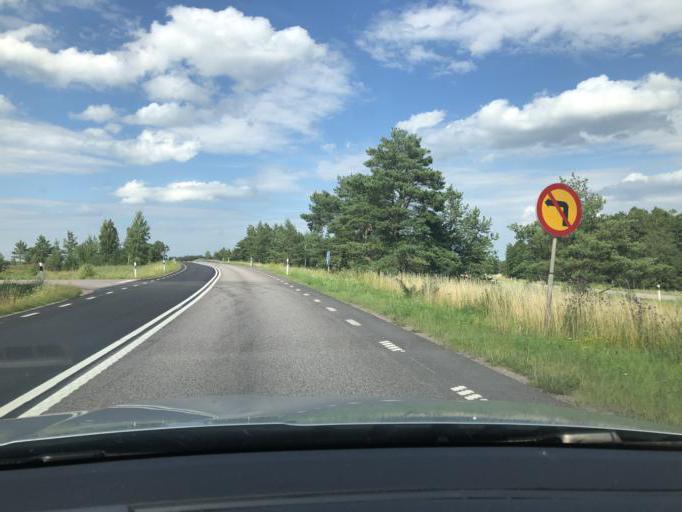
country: SE
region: OEstergoetland
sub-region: Mjolby Kommun
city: Mjolby
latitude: 58.3403
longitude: 15.1703
